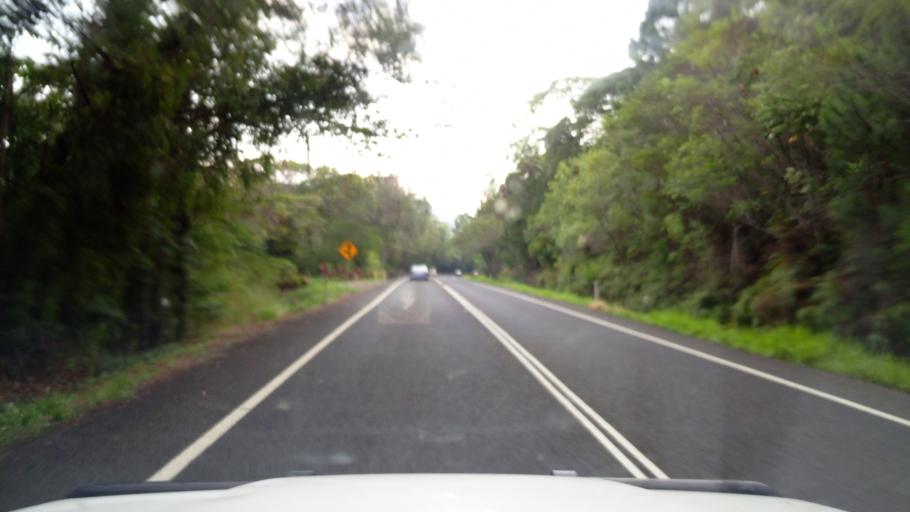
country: AU
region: Queensland
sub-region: Tablelands
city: Kuranda
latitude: -16.8343
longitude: 145.6196
